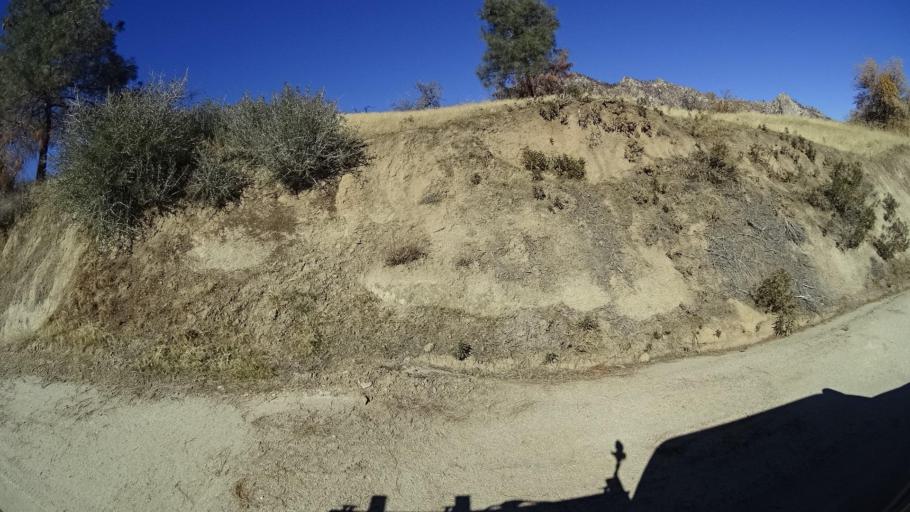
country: US
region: California
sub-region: Kern County
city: Alta Sierra
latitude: 35.7143
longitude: -118.5178
